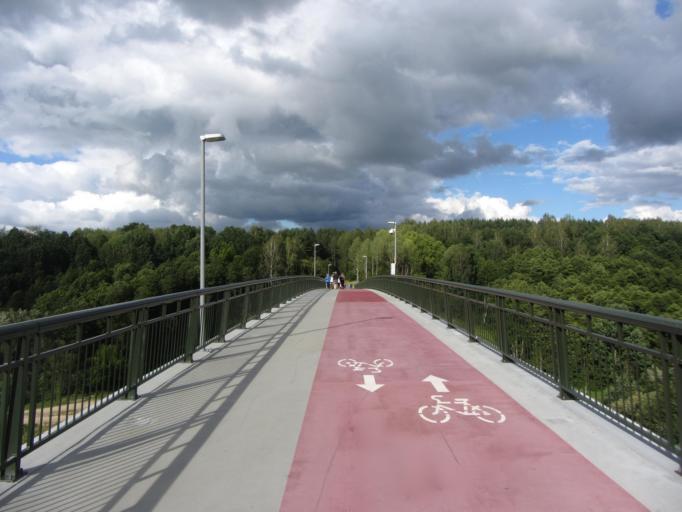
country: LT
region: Alytaus apskritis
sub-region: Alytus
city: Alytus
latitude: 54.3936
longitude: 24.0815
